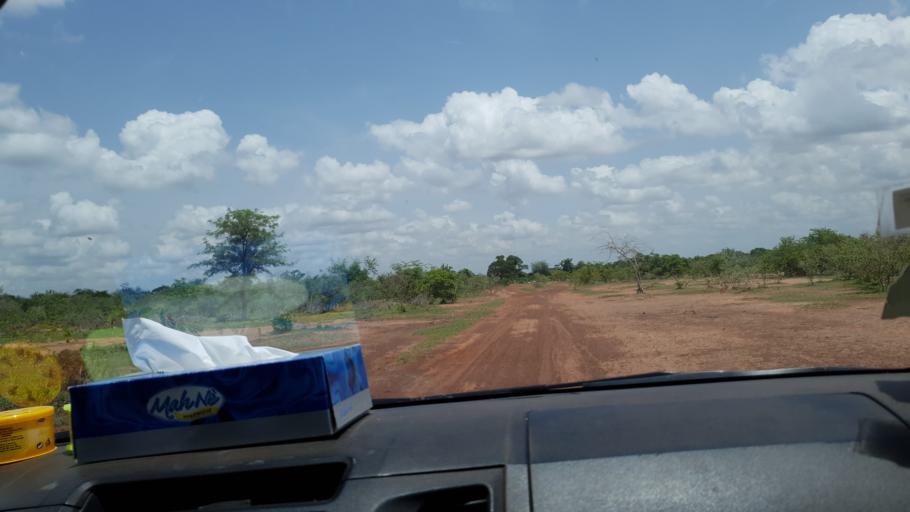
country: ML
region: Koulikoro
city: Banamba
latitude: 13.3782
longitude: -7.2112
